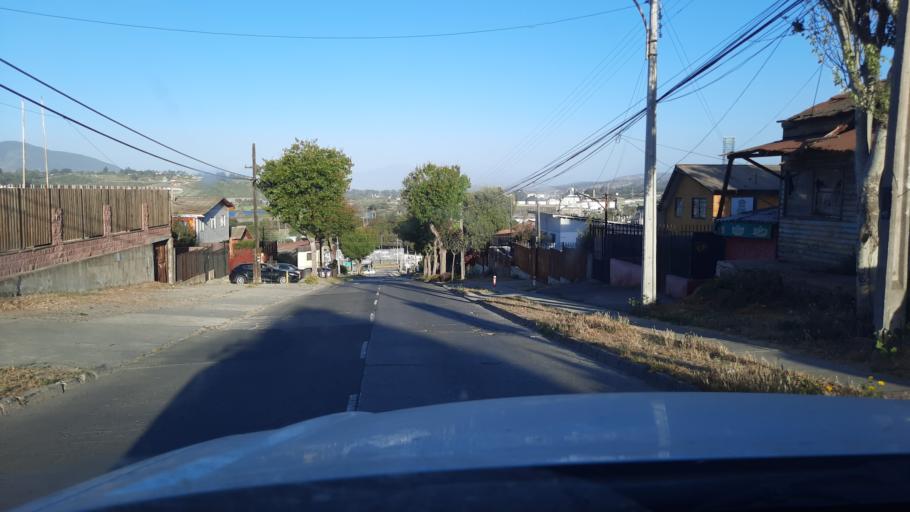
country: CL
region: Valparaiso
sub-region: Provincia de Valparaiso
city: Vina del Mar
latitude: -32.9238
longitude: -71.5088
